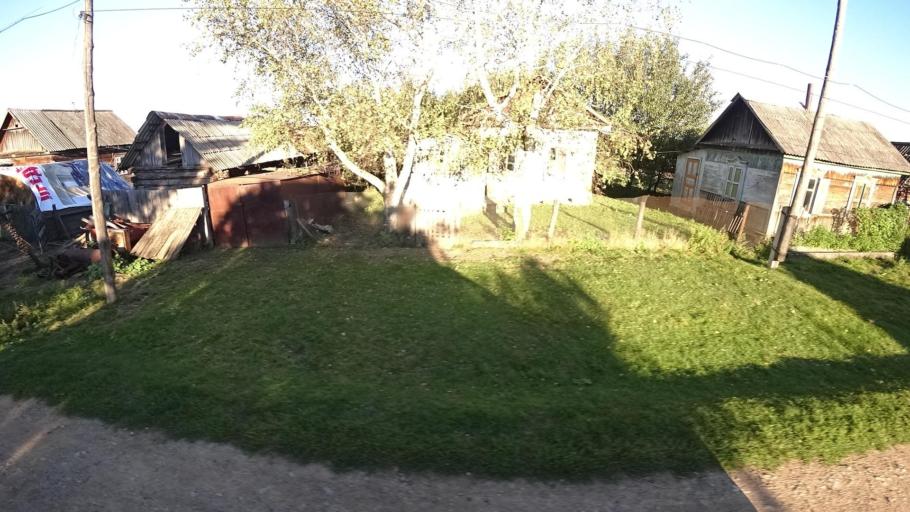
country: RU
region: Primorskiy
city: Kirovskiy
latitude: 44.8330
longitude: 133.5756
